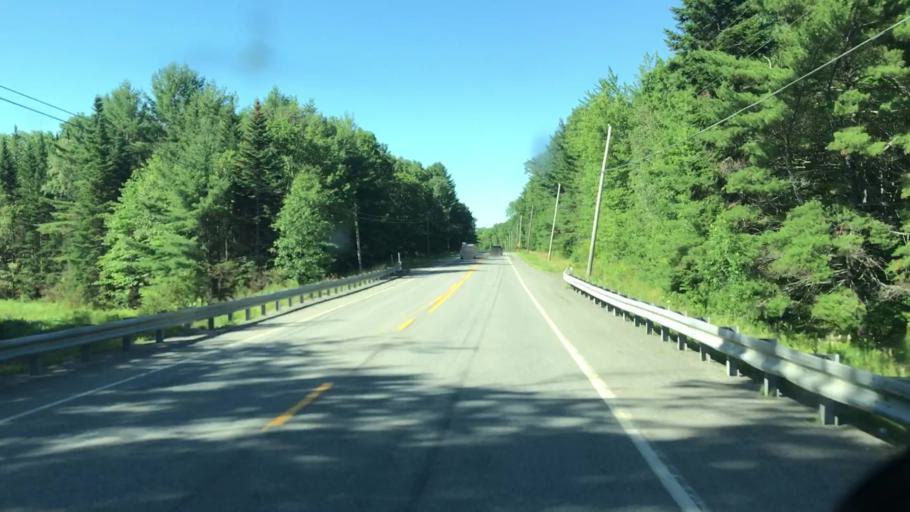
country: US
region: Maine
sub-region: Penobscot County
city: Howland
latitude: 45.2759
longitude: -68.6346
